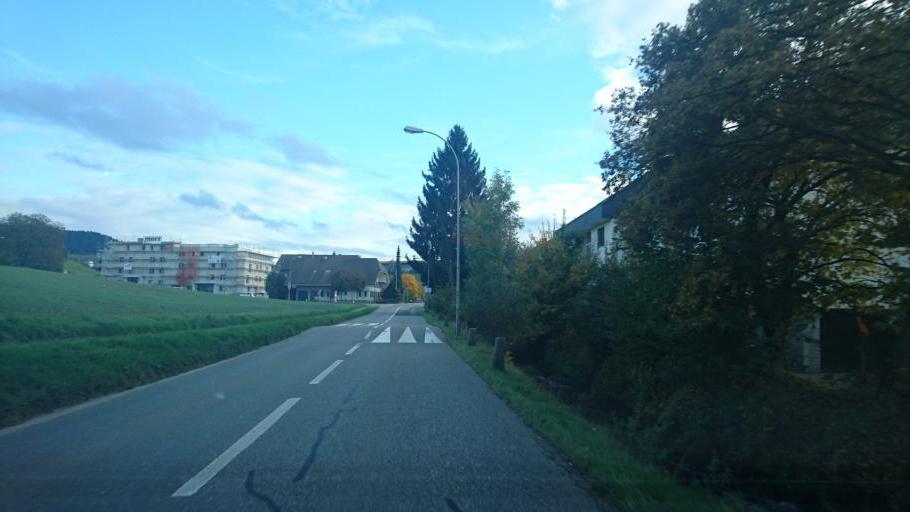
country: CH
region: Bern
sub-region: Bern-Mittelland District
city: Biglen
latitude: 46.9295
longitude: 7.6205
